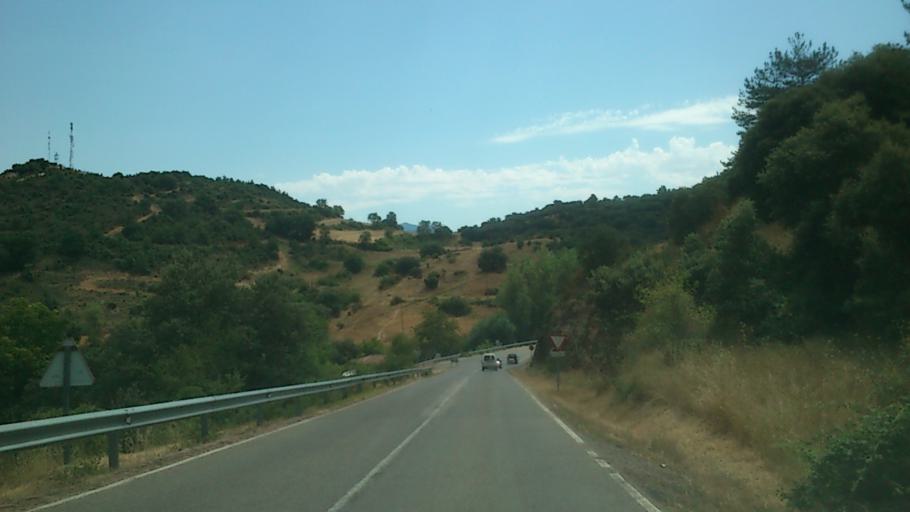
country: ES
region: Castille and Leon
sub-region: Provincia de Burgos
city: Frias
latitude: 42.7601
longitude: -3.2983
